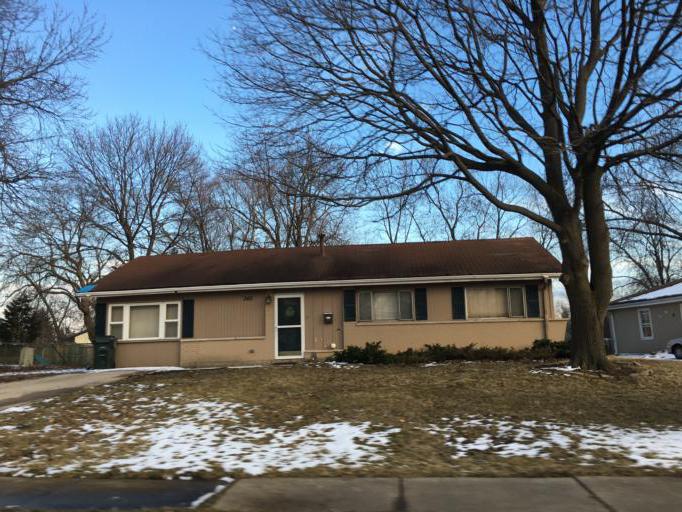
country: US
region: Illinois
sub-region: Cook County
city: Schaumburg
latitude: 42.0323
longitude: -88.0891
